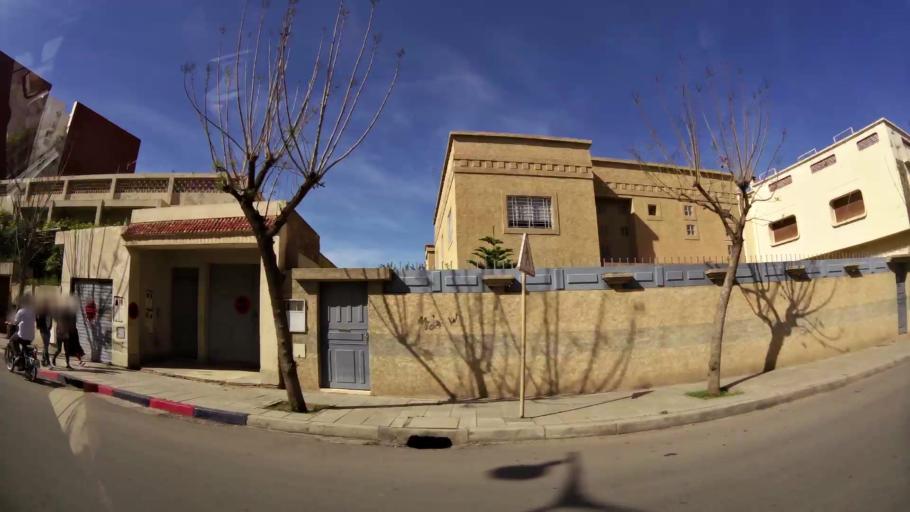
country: MA
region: Oriental
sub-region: Oujda-Angad
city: Oujda
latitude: 34.6726
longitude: -1.9116
